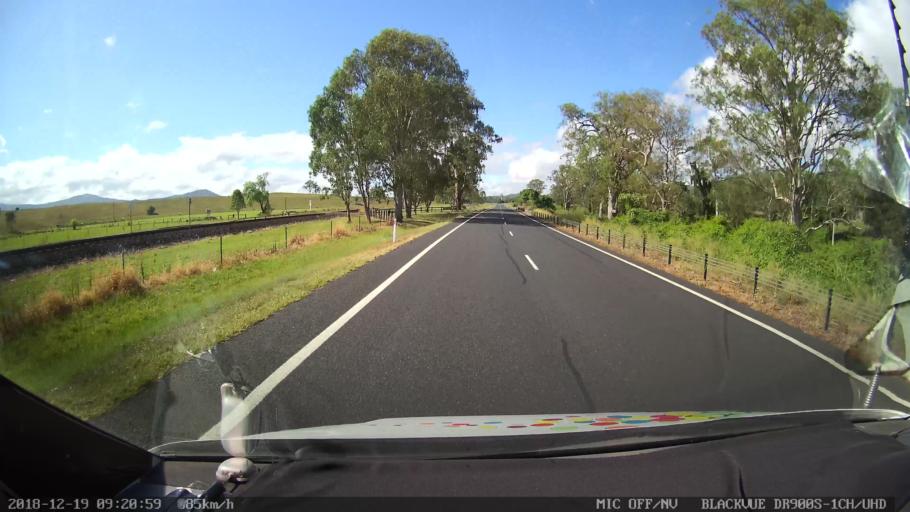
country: AU
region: New South Wales
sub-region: Kyogle
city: Kyogle
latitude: -28.5780
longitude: 152.9825
